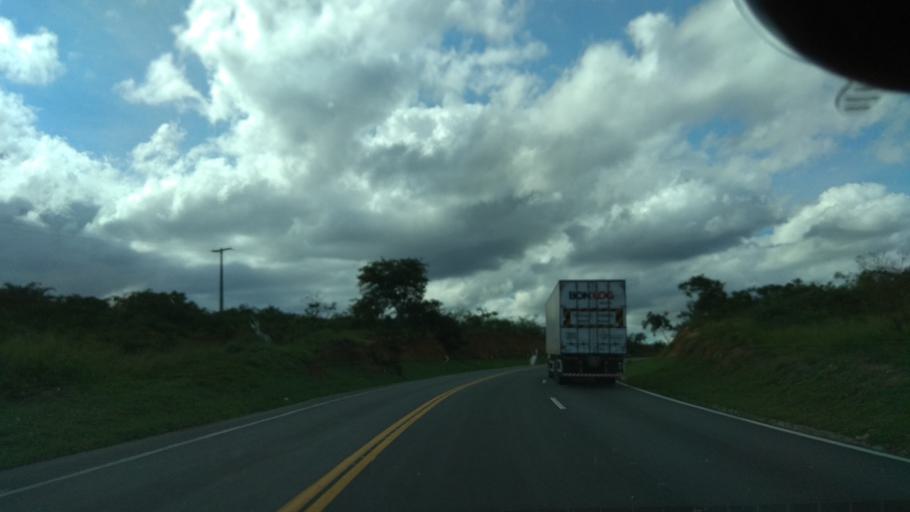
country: BR
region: Bahia
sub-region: Santa Ines
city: Santa Ines
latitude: -13.1060
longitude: -39.9952
